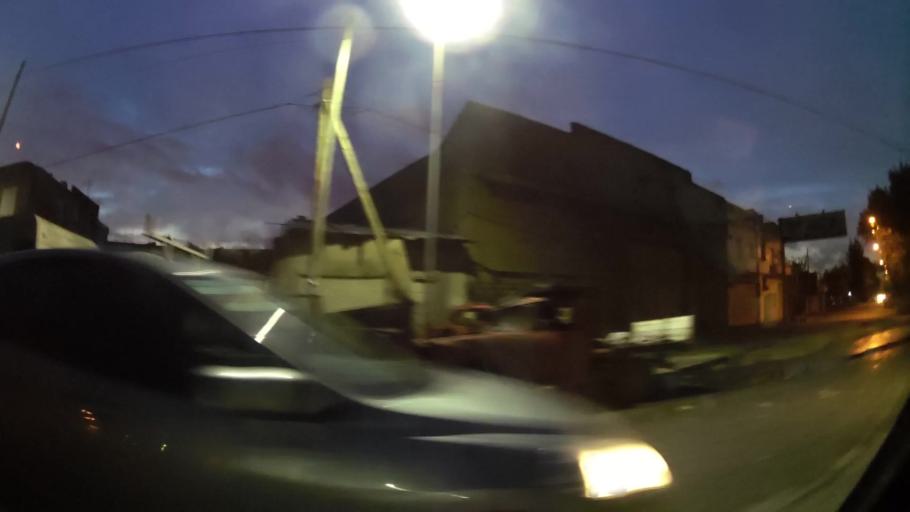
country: AR
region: Buenos Aires
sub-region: Partido de Lanus
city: Lanus
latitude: -34.7348
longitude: -58.3495
